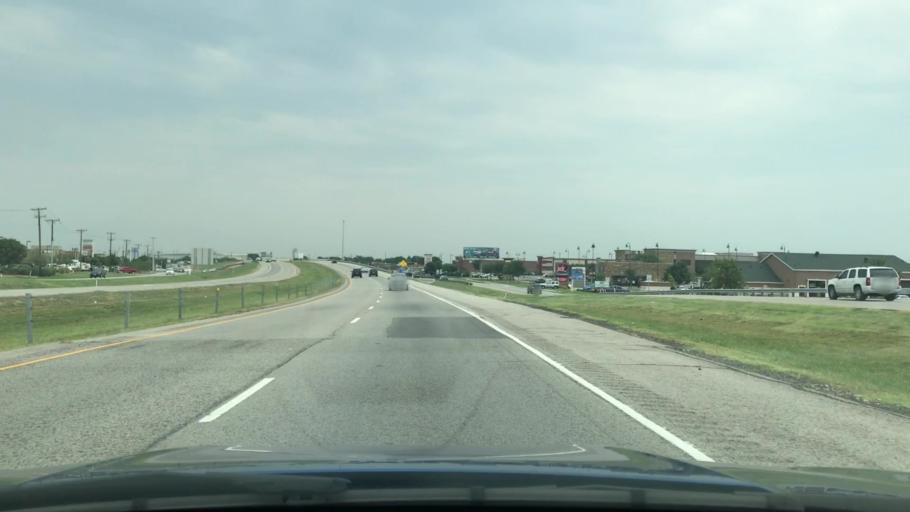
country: US
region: Texas
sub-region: Kaufman County
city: Forney
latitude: 32.7449
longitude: -96.4528
